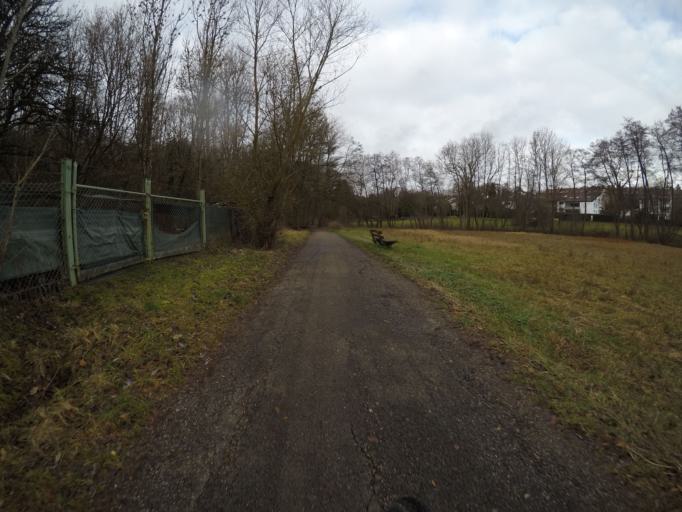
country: DE
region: Baden-Wuerttemberg
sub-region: Regierungsbezirk Stuttgart
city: Steinenbronn
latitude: 48.7278
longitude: 9.0907
